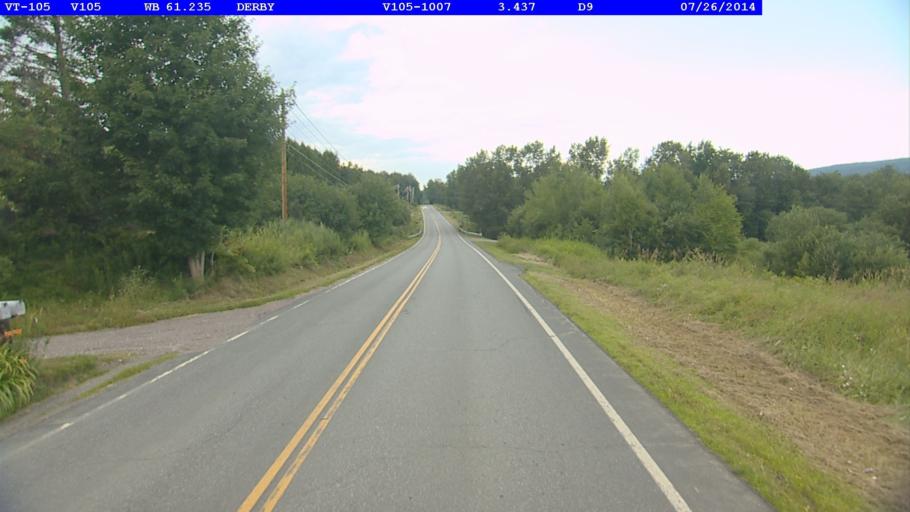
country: US
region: Vermont
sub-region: Orleans County
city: Newport
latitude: 44.9150
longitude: -72.0999
